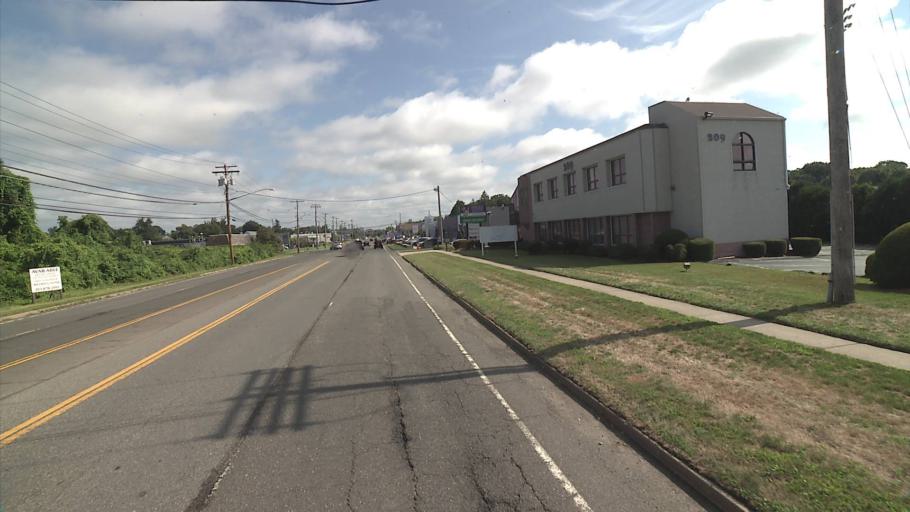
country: US
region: Connecticut
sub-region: New Haven County
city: City of Milford (balance)
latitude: 41.2200
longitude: -73.0742
